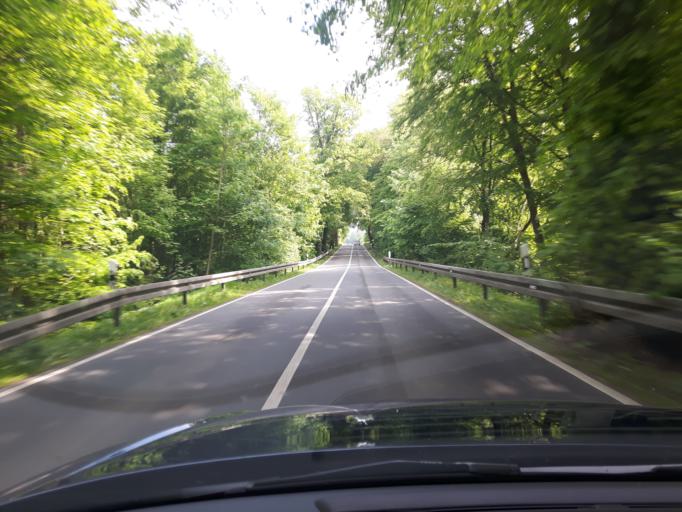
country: DE
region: Mecklenburg-Vorpommern
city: Gross Wokern
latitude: 53.6331
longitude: 12.4752
